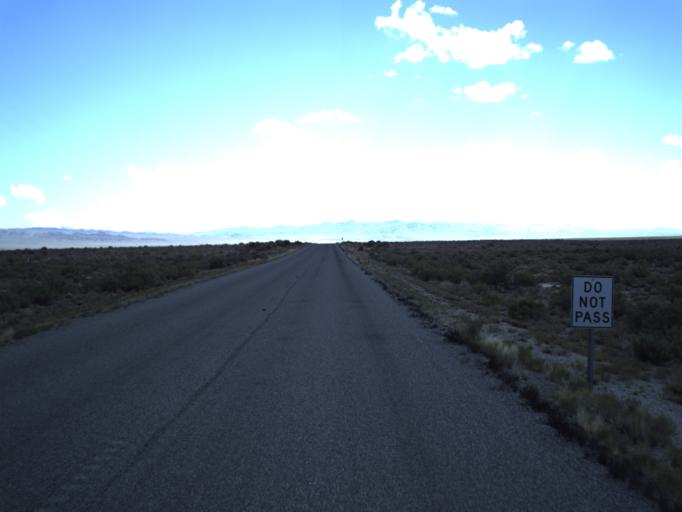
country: US
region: Nevada
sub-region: White Pine County
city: McGill
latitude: 39.0540
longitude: -114.0088
